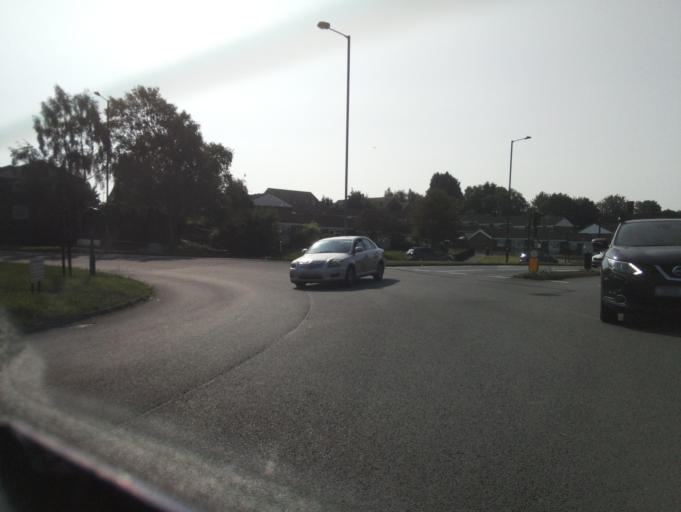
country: GB
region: England
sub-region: Walsall
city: Streetly
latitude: 52.5560
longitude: -1.8991
